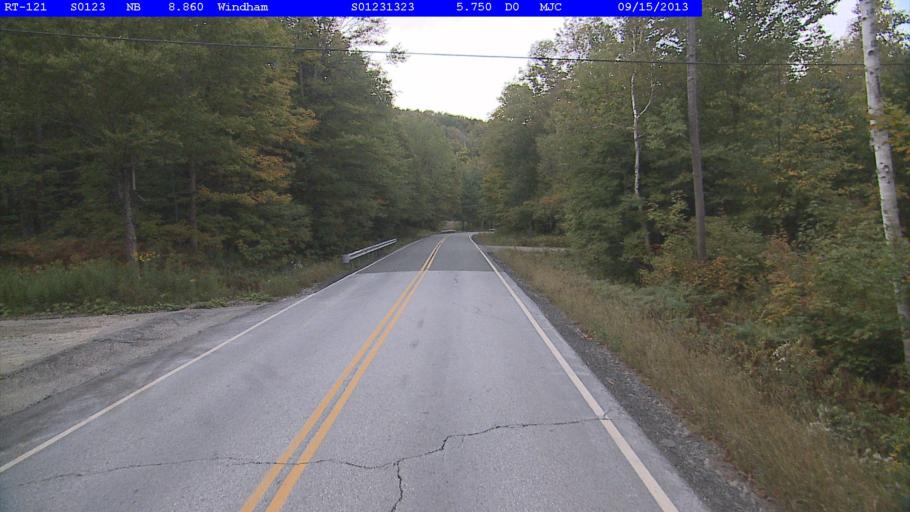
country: US
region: Vermont
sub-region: Windsor County
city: Chester
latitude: 43.1997
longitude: -72.7301
